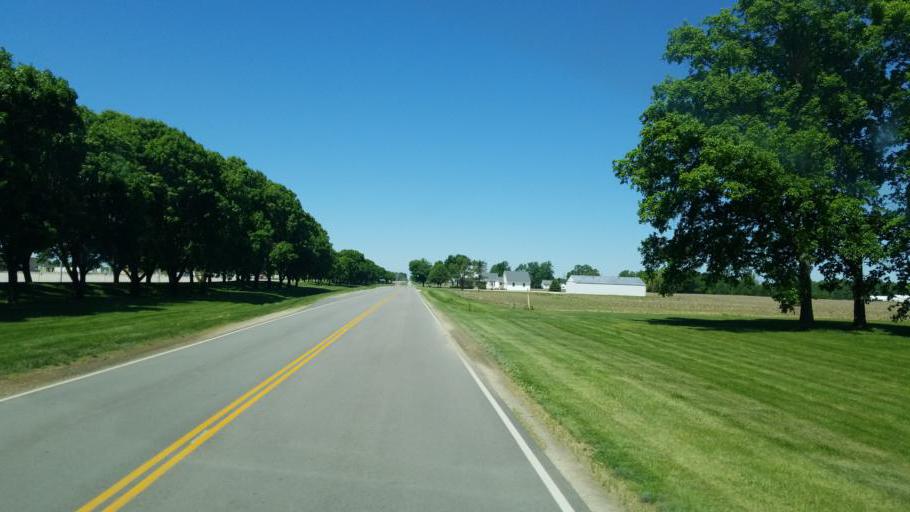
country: US
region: Ohio
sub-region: Shelby County
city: Anna
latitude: 40.3805
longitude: -84.1918
